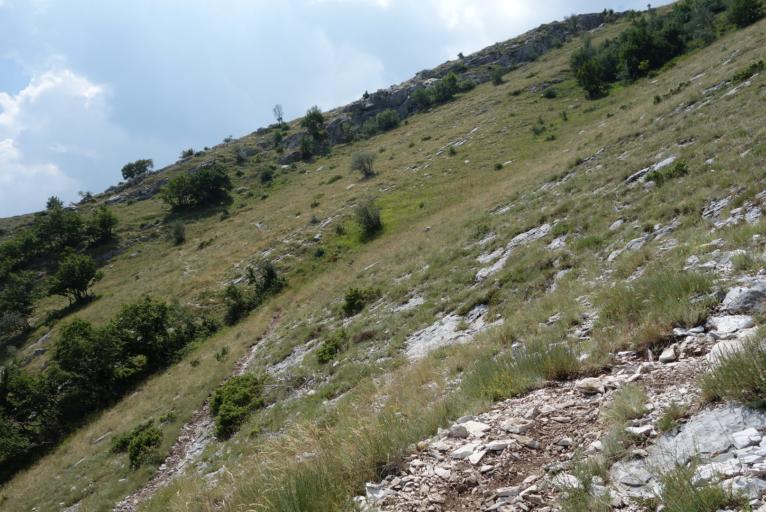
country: AL
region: Gjirokaster
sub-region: Rrethi i Permetit
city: Permet
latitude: 40.2051
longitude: 20.3351
